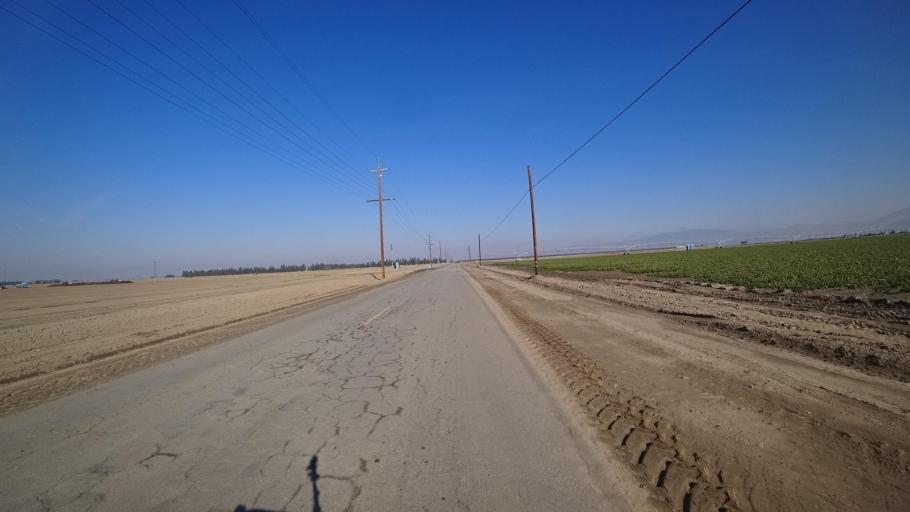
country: US
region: California
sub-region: Kern County
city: Arvin
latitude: 35.1272
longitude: -118.8776
